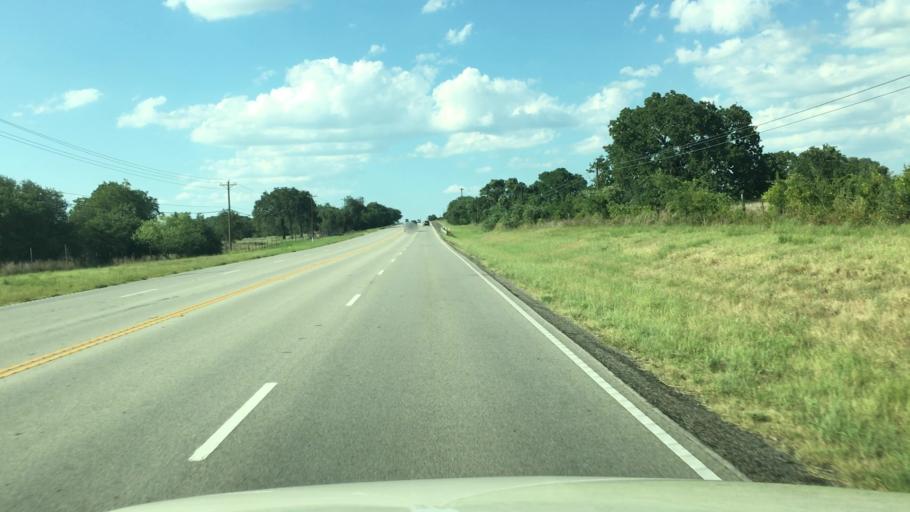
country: US
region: Texas
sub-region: Blanco County
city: Johnson City
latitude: 30.3463
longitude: -98.3804
